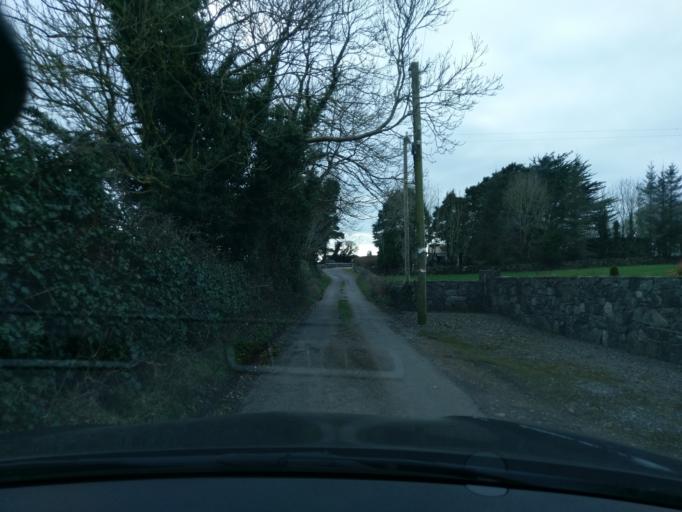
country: IE
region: Connaught
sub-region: County Galway
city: Oranmore
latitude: 53.2024
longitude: -8.9131
